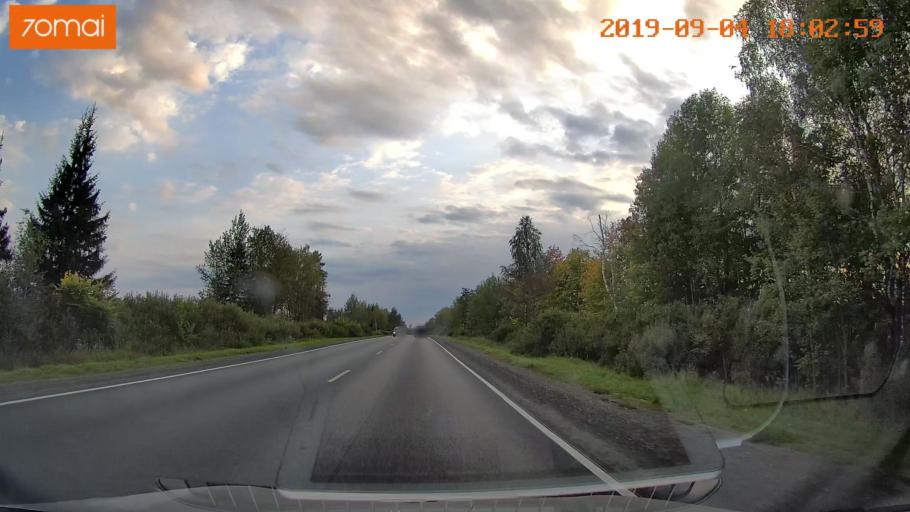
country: RU
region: Moskovskaya
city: Il'inskiy Pogost
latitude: 55.4676
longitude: 38.8578
